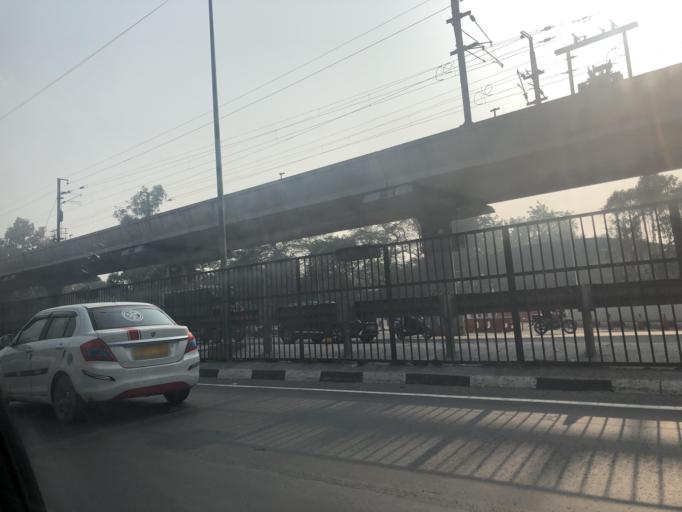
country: IN
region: NCT
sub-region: Central Delhi
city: Karol Bagh
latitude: 28.5890
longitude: 77.1533
